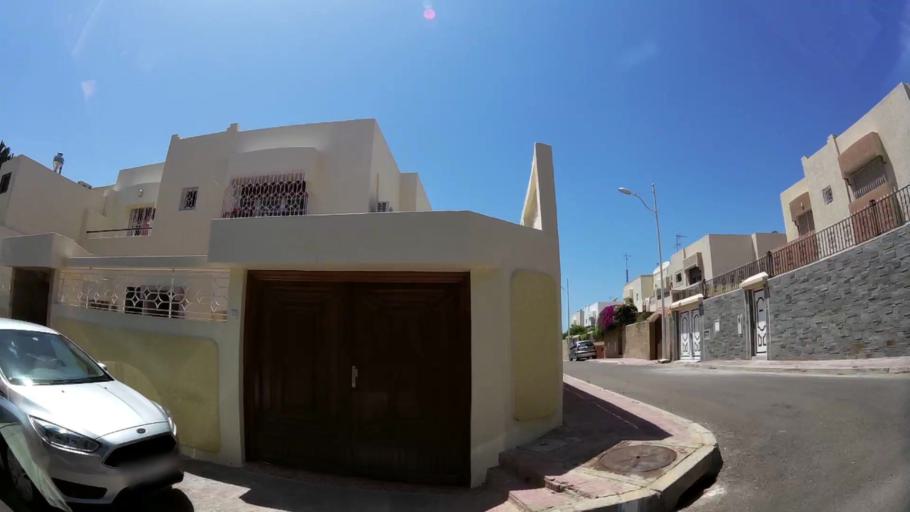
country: MA
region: Souss-Massa-Draa
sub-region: Agadir-Ida-ou-Tnan
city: Agadir
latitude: 30.4324
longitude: -9.5850
